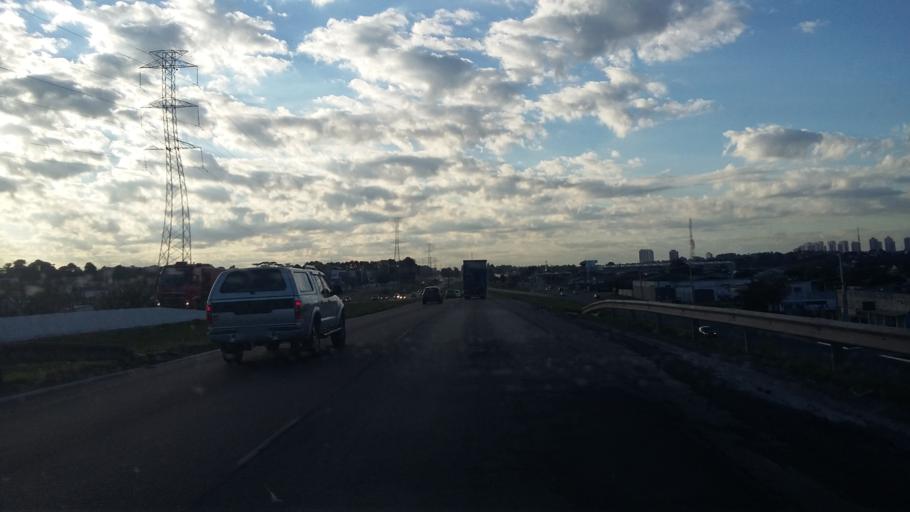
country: BR
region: Parana
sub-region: Curitiba
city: Curitiba
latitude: -25.4835
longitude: -49.3479
